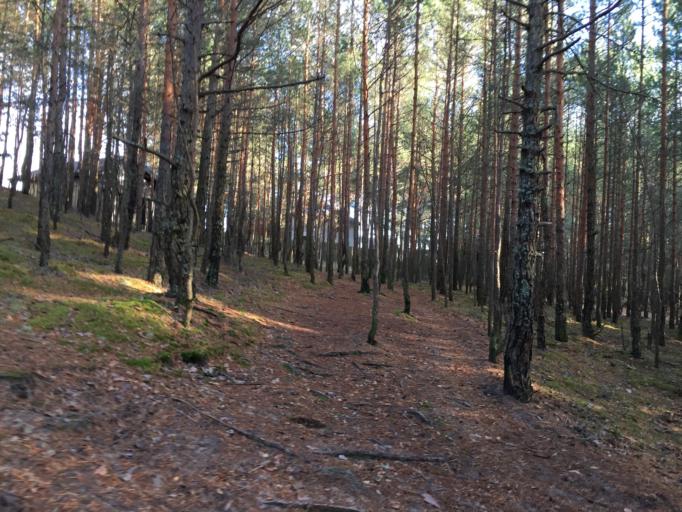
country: LV
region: Carnikava
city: Carnikava
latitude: 57.1532
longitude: 24.2799
